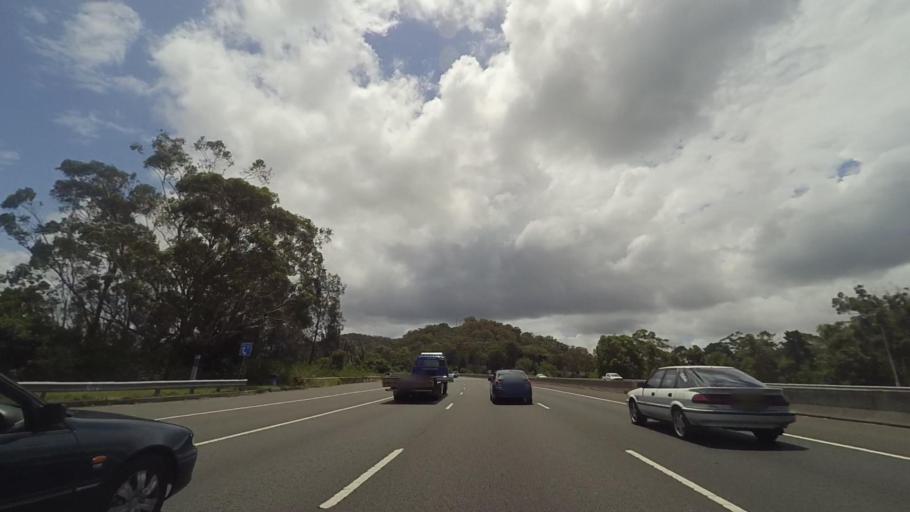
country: AU
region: New South Wales
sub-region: Hornsby Shire
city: Berowra
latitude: -33.5306
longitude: 151.2003
